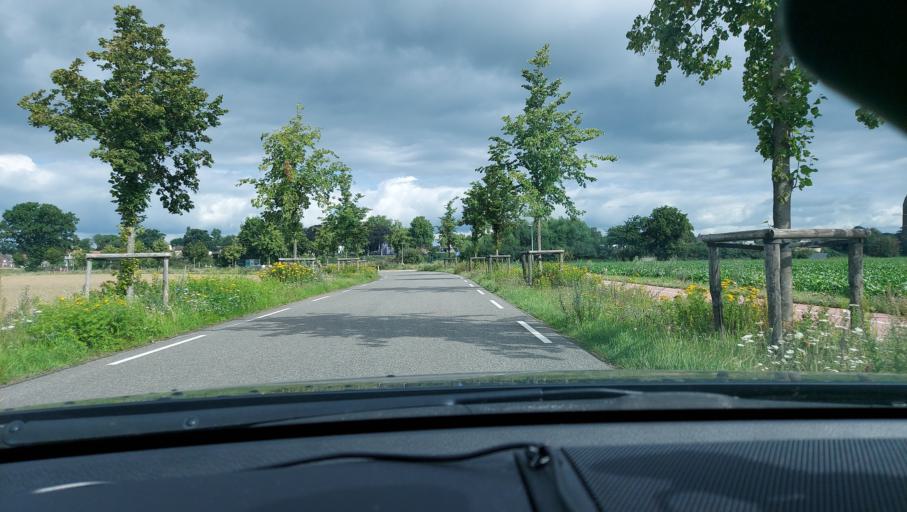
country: NL
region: Limburg
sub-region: Gemeente Beesel
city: Beesel
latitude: 51.2857
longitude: 6.0540
